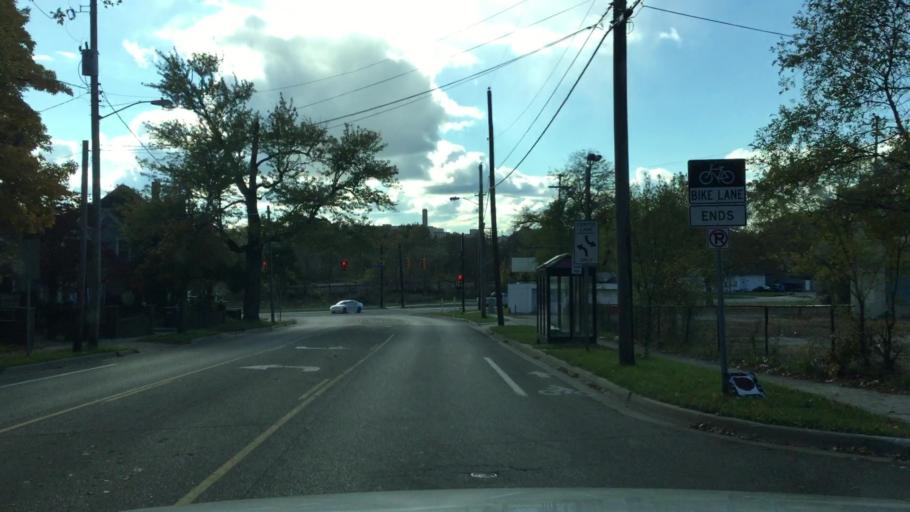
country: US
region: Michigan
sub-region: Kalamazoo County
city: Eastwood
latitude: 42.2958
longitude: -85.5642
